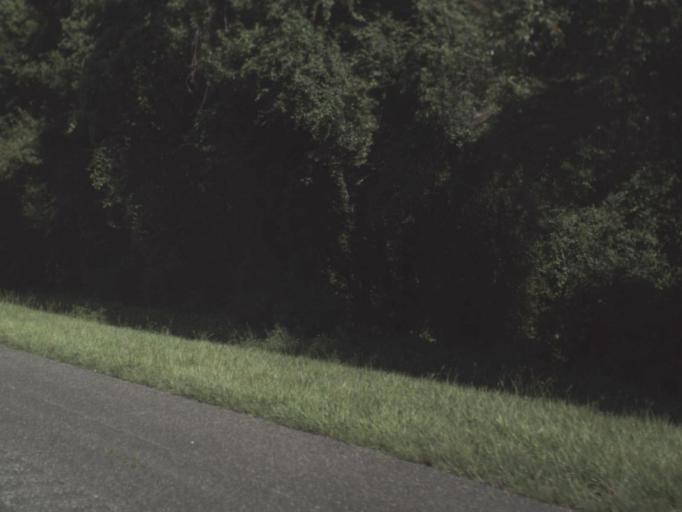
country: US
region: Florida
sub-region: Suwannee County
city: Wellborn
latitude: 30.2754
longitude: -82.8021
